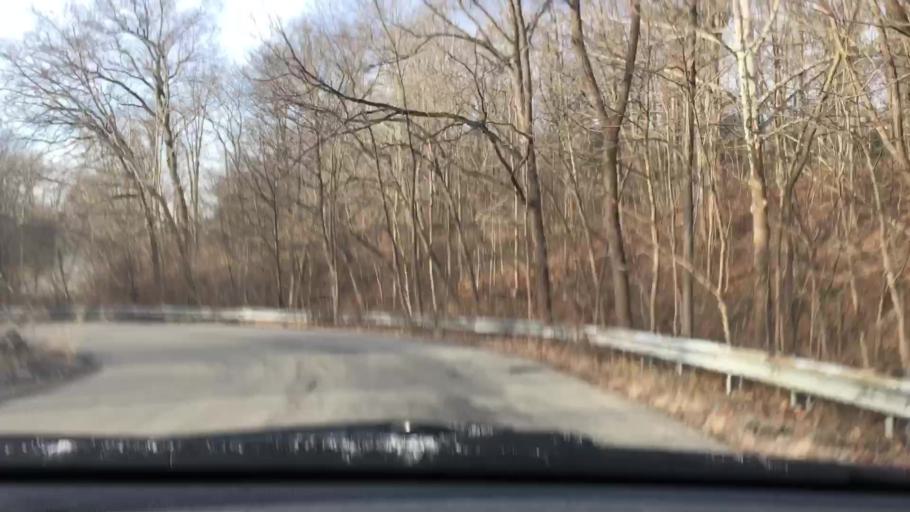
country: US
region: Pennsylvania
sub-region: Westmoreland County
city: Collinsburg
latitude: 40.2610
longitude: -79.7268
